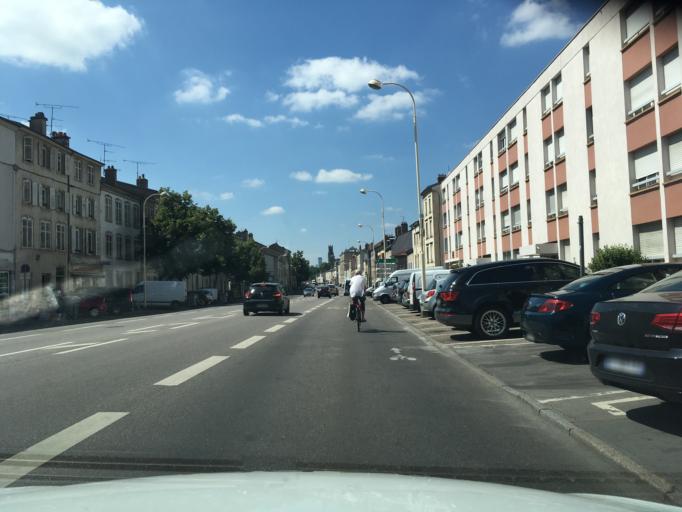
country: FR
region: Lorraine
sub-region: Departement de Meurthe-et-Moselle
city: Jarville-la-Malgrange
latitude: 48.6777
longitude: 6.1987
